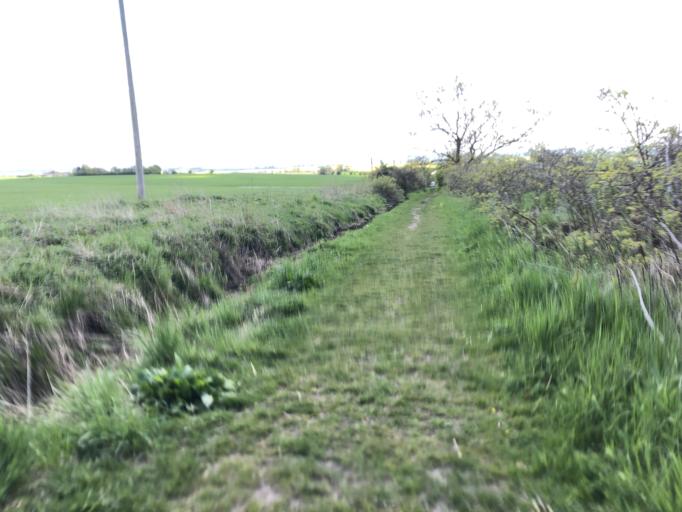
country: SE
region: Skane
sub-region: Lunds Kommun
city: Lund
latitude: 55.6936
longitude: 13.2872
